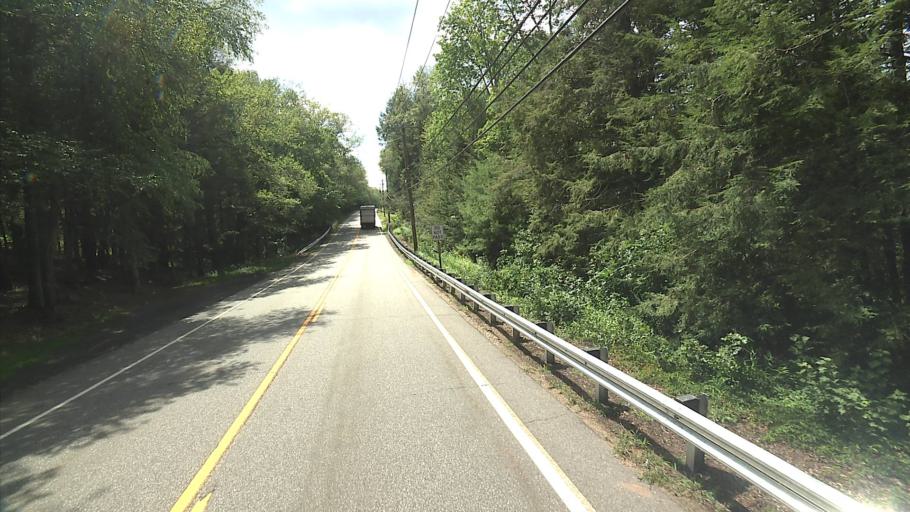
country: US
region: Connecticut
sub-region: Tolland County
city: Stafford
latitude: 41.9601
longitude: -72.2549
